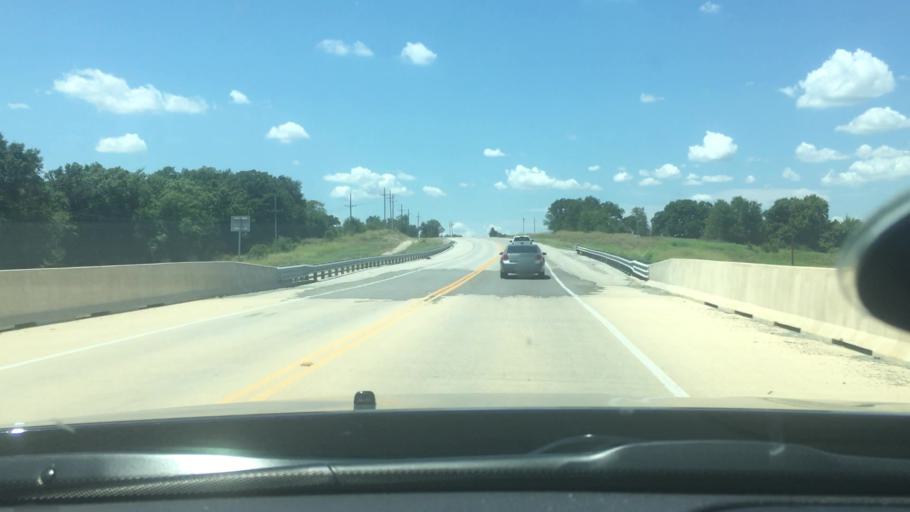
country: US
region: Oklahoma
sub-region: Bryan County
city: Durant
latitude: 33.9978
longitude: -96.2415
